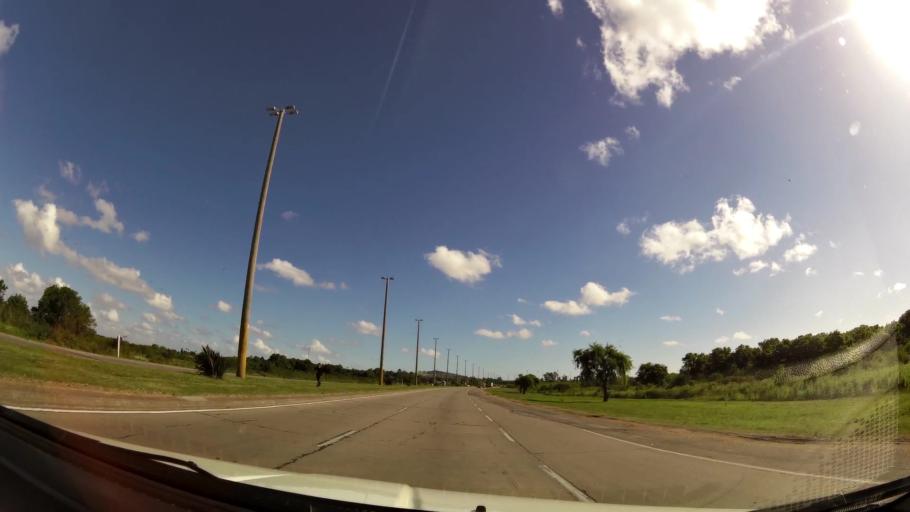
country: UY
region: Montevideo
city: Montevideo
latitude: -34.8510
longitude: -56.2544
